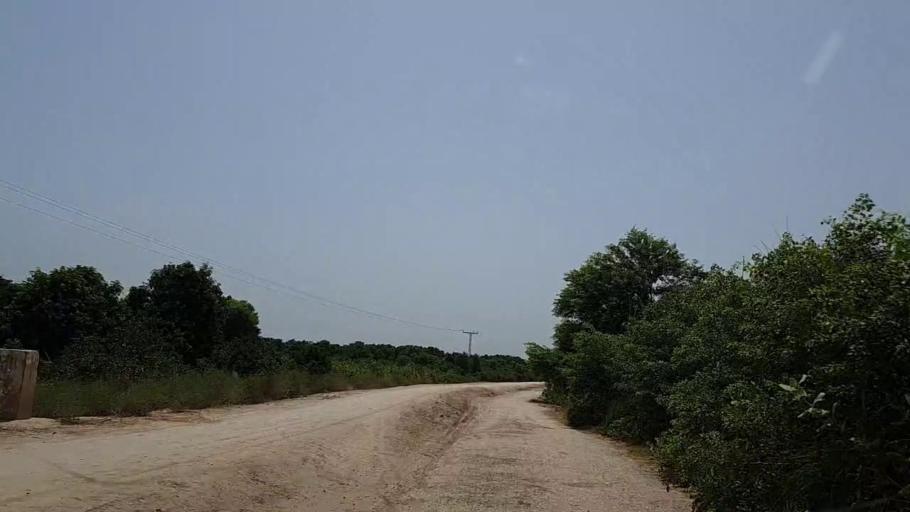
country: PK
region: Sindh
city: Tharu Shah
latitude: 26.9993
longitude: 68.1180
